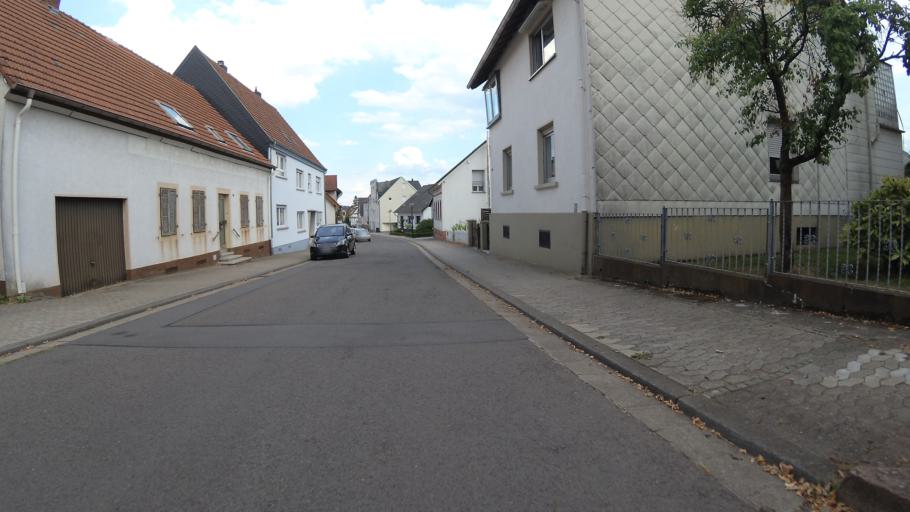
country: DE
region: Saarland
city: Bexbach
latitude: 49.3163
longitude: 7.2705
